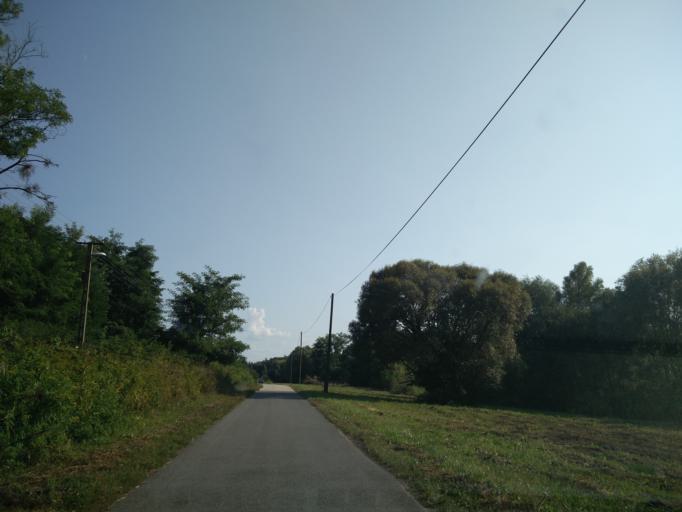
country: HU
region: Zala
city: Zalaegerszeg
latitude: 46.8714
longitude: 16.8489
